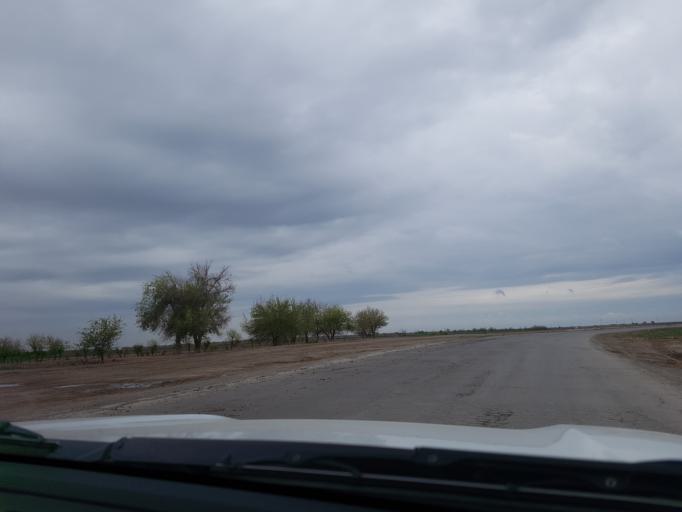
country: TM
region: Mary
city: Bayramaly
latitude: 37.5775
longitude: 62.1628
